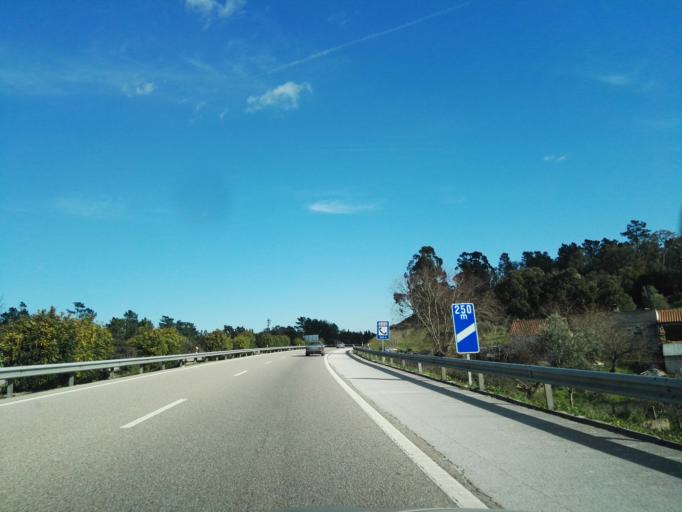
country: PT
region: Santarem
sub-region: Constancia
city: Constancia
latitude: 39.4857
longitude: -8.3621
